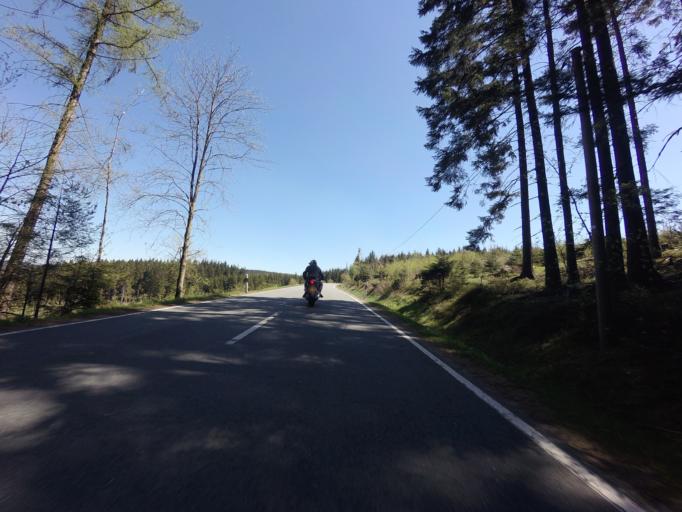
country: DE
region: North Rhine-Westphalia
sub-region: Regierungsbezirk Arnsberg
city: Kirchhundem
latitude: 51.0708
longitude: 8.1911
